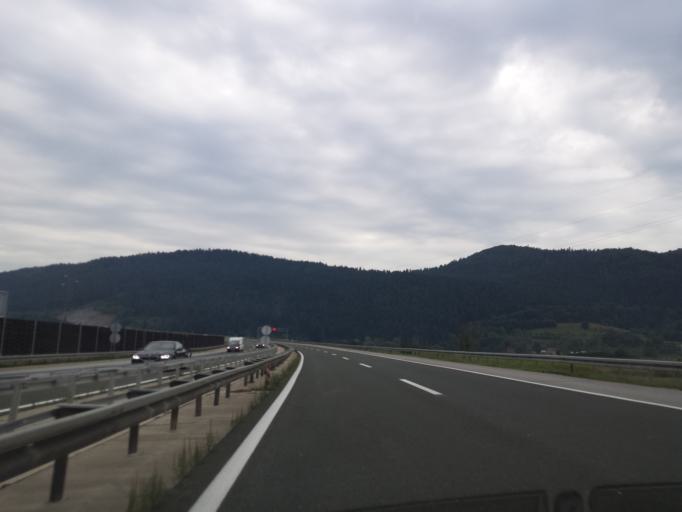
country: HR
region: Licko-Senjska
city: Otocac
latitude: 44.8679
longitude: 15.2076
